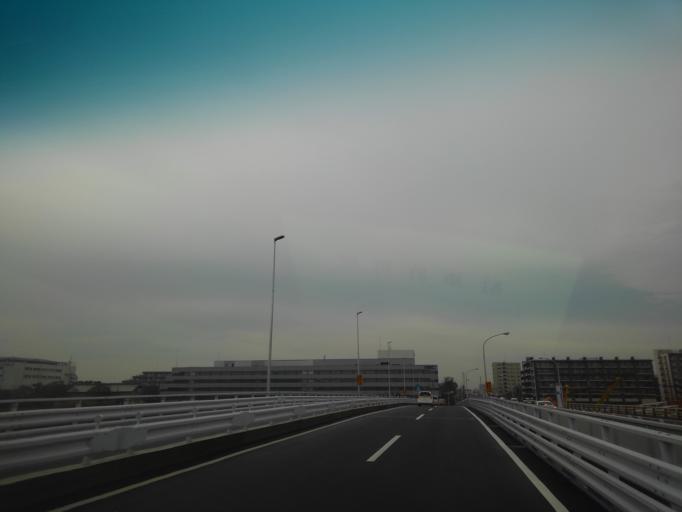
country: JP
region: Tokyo
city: Kokubunji
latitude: 35.6531
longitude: 139.4549
